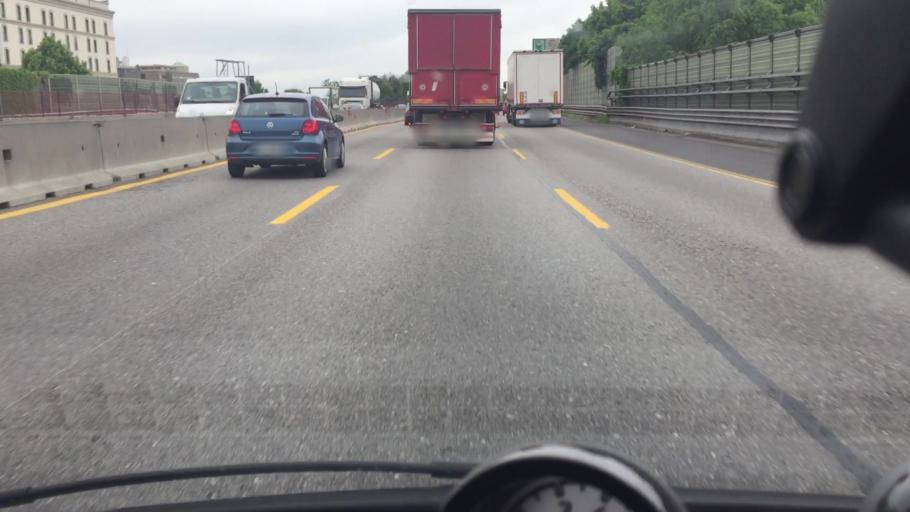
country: IT
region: Lombardy
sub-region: Citta metropolitana di Milano
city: Cinisello Balsamo
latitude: 45.5493
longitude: 9.2205
